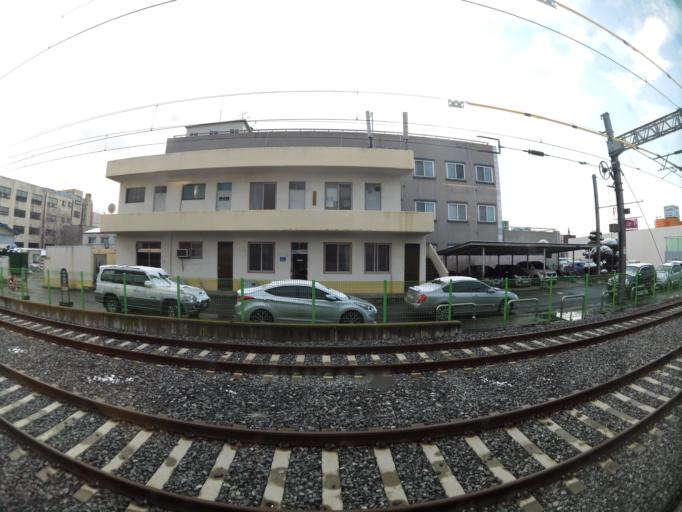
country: KR
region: Daejeon
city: Daejeon
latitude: 36.3311
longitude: 127.4346
